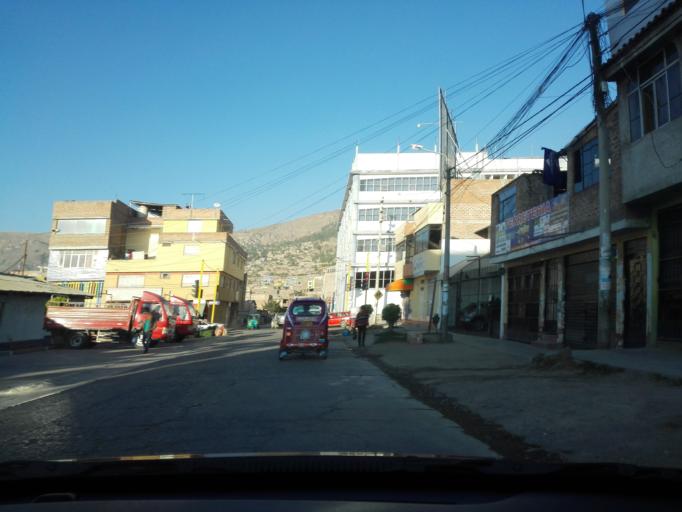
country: PE
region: Ayacucho
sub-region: Provincia de Huamanga
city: Ayacucho
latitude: -13.1484
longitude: -74.2274
